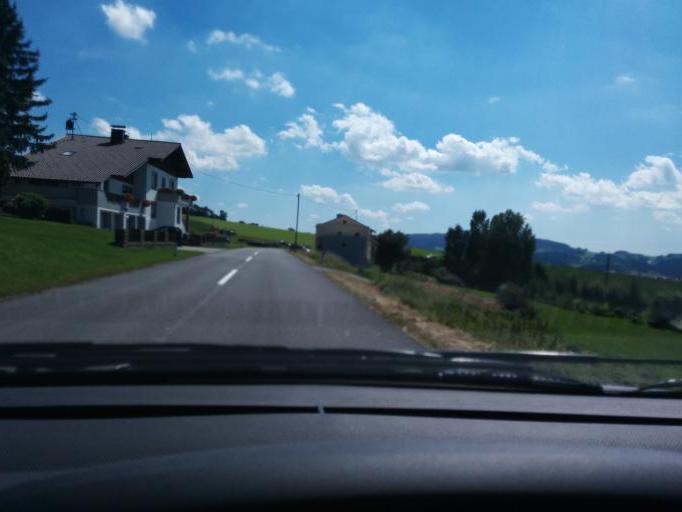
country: AT
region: Upper Austria
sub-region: Politischer Bezirk Rohrbach
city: Ulrichsberg
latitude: 48.6958
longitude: 13.9044
